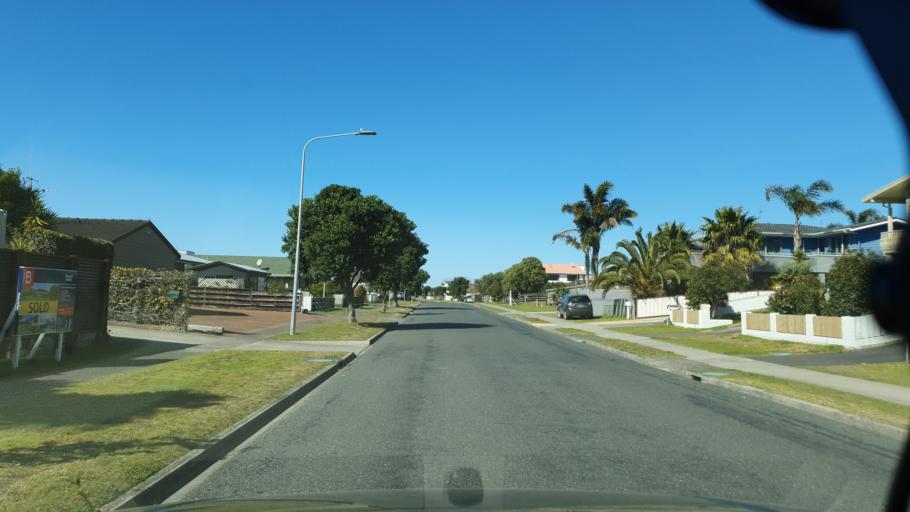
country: NZ
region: Bay of Plenty
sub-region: Tauranga City
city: Tauranga
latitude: -37.6992
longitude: 176.2867
